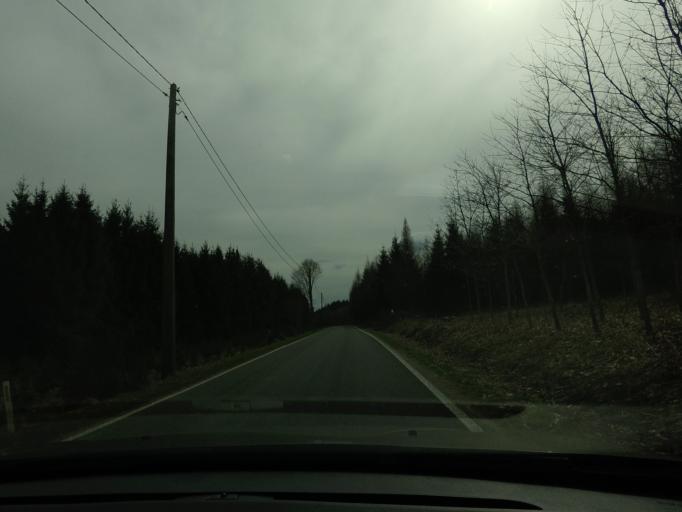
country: BE
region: Wallonia
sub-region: Province de Liege
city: Aywaille
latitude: 50.4174
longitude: 5.7157
